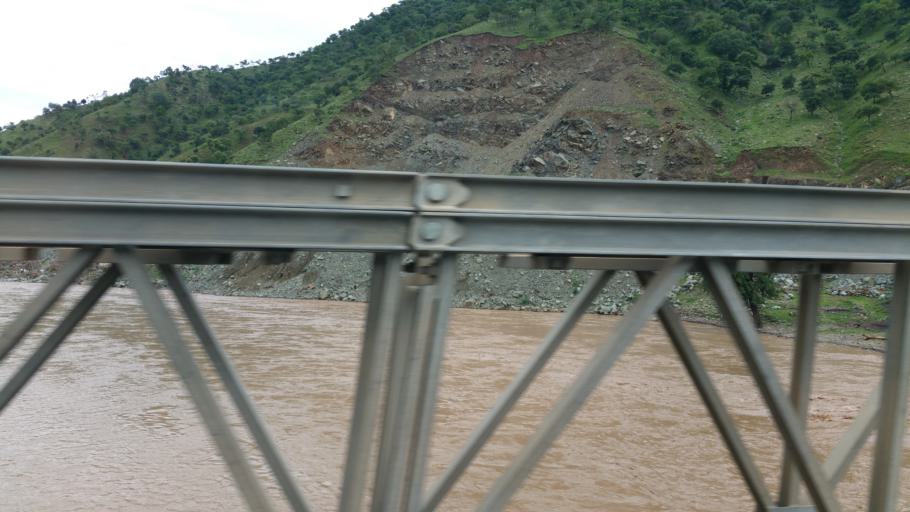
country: ET
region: Tigray
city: Inda Silase
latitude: 13.7369
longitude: 38.1980
